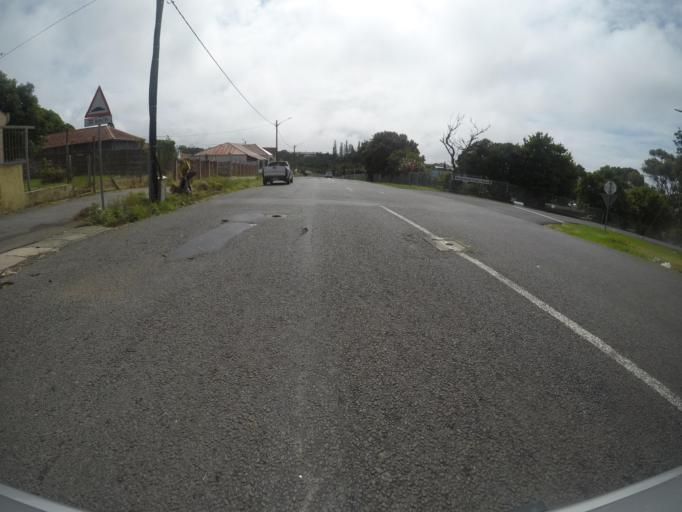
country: ZA
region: Eastern Cape
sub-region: Buffalo City Metropolitan Municipality
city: East London
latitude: -33.0020
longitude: 27.9108
